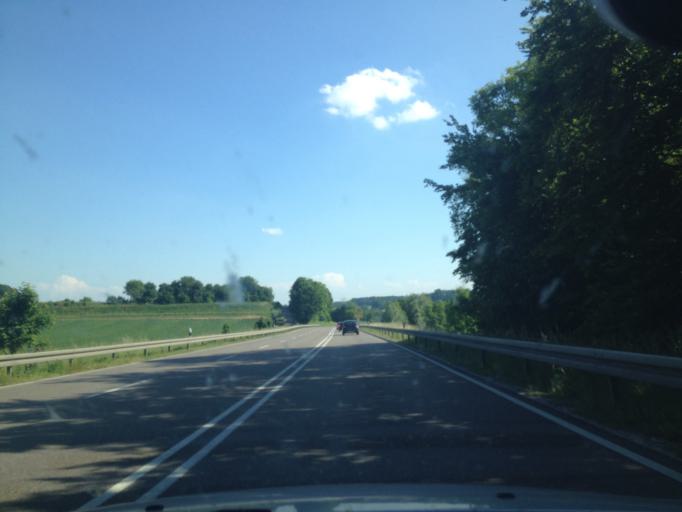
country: DE
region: Bavaria
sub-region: Swabia
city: Aichach
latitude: 48.4456
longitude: 11.1431
